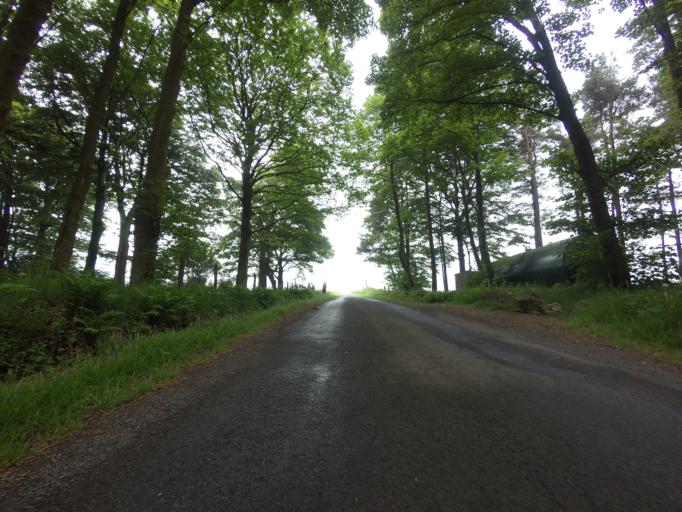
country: GB
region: Scotland
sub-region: Perth and Kinross
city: Milnathort
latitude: 56.2464
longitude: -3.3387
